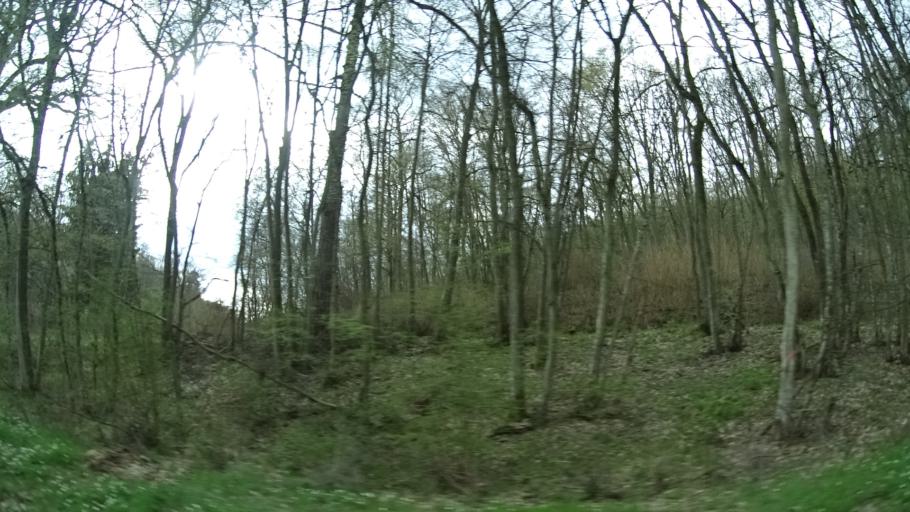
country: DE
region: Rheinland-Pfalz
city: Allenfeld
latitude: 49.8527
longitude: 7.6588
